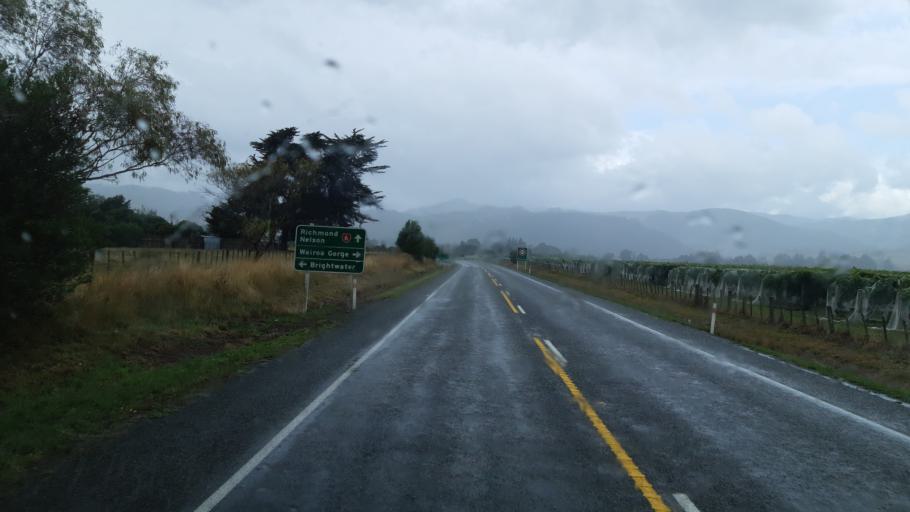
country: NZ
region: Tasman
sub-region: Tasman District
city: Brightwater
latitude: -41.3792
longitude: 173.1078
